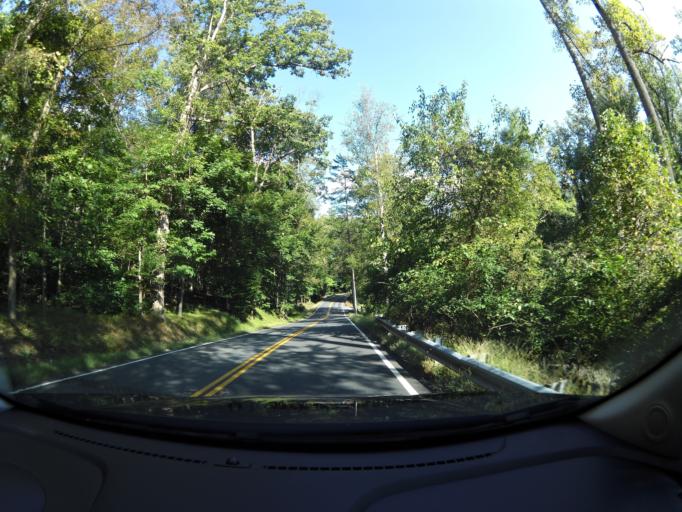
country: US
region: Virginia
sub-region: Fairfax County
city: Great Falls
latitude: 38.9783
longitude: -77.2505
